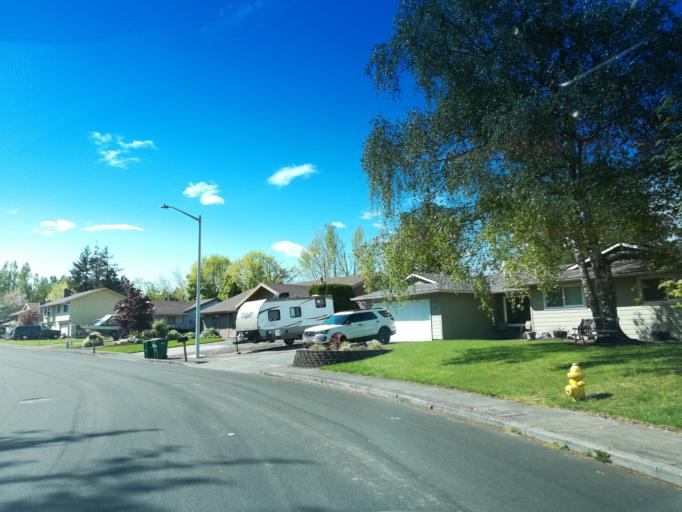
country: US
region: Oregon
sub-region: Multnomah County
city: Troutdale
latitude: 45.5271
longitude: -122.3828
